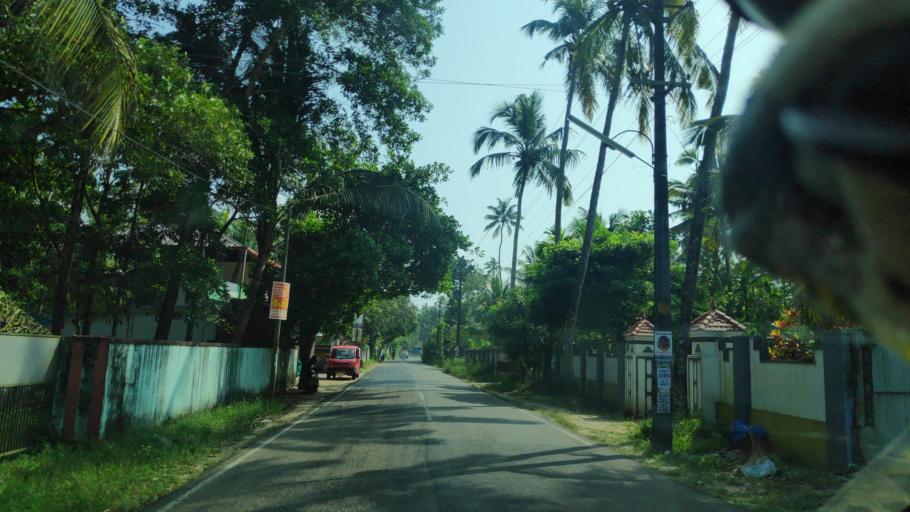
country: IN
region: Kerala
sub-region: Alappuzha
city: Shertallai
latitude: 9.6184
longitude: 76.3006
